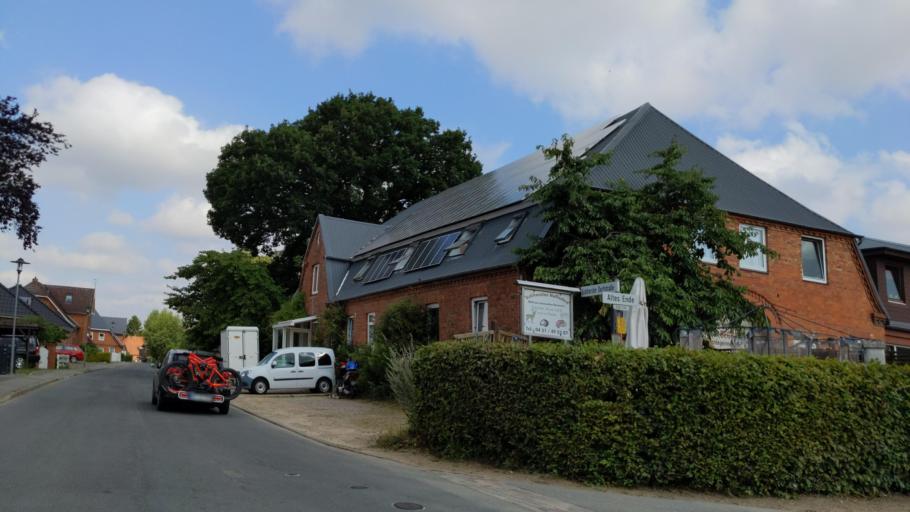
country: DE
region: Schleswig-Holstein
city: Stockelsdorf
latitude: 53.8938
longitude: 10.6042
